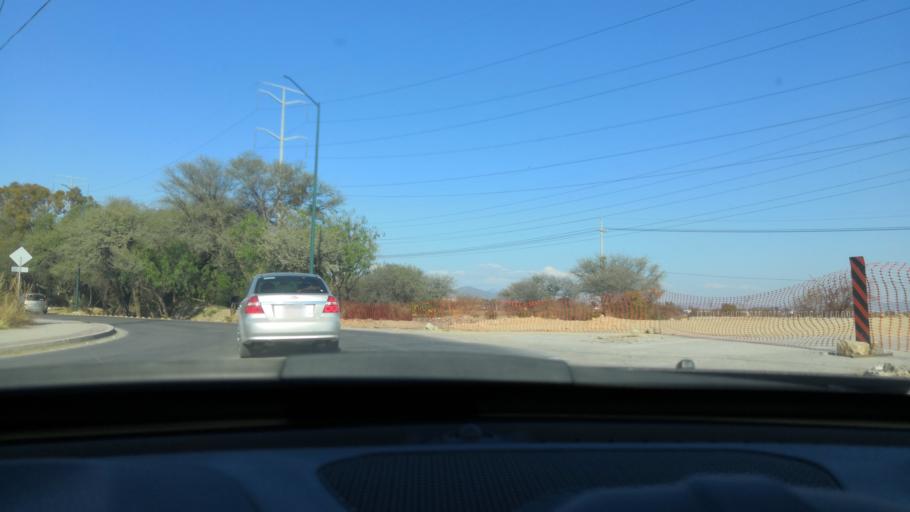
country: MX
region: Guanajuato
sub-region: Leon
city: Fraccionamiento Paraiso Real
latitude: 21.0590
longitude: -101.6092
